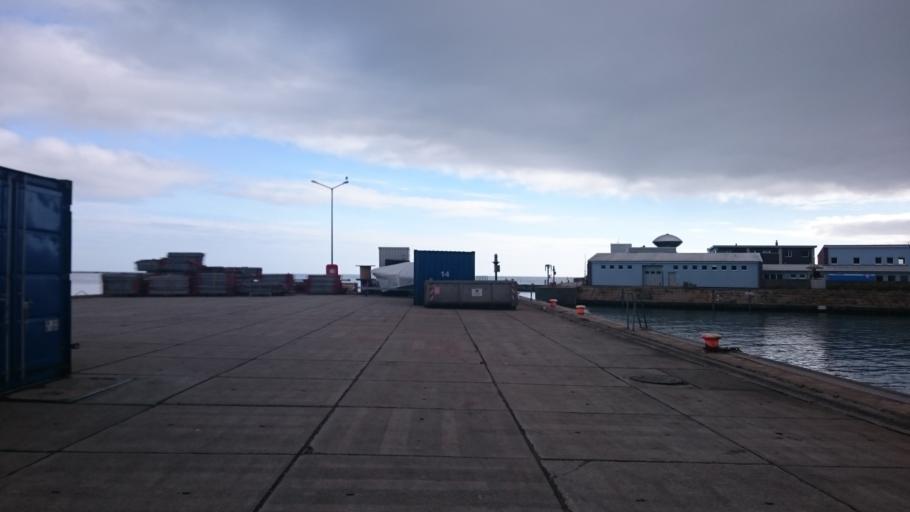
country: DE
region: Schleswig-Holstein
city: Helgoland
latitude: 54.1790
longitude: 7.8892
